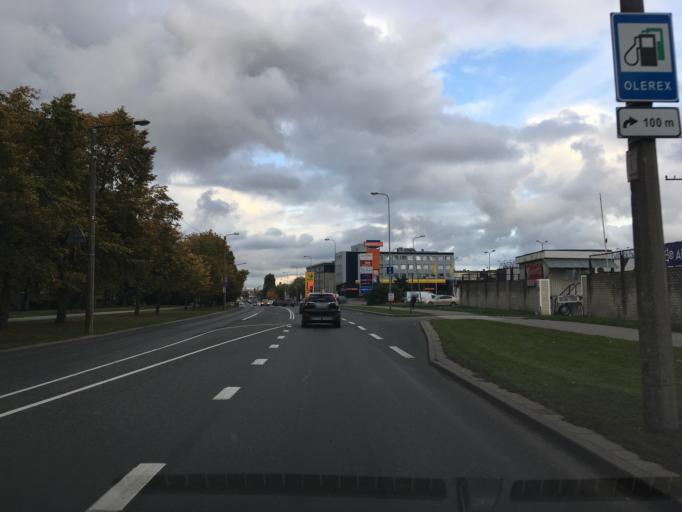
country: EE
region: Harju
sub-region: Tallinna linn
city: Kose
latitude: 59.4324
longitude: 24.8204
